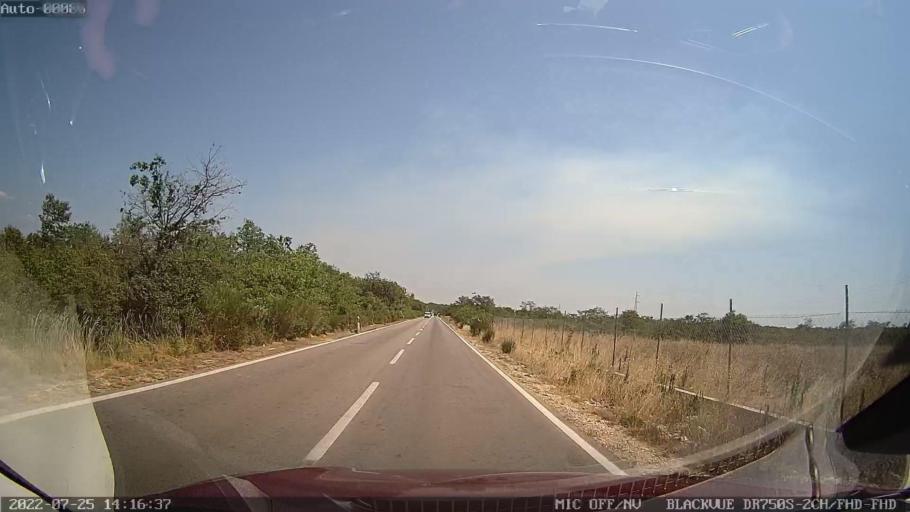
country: HR
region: Zadarska
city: Zadar
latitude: 44.1909
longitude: 15.2626
